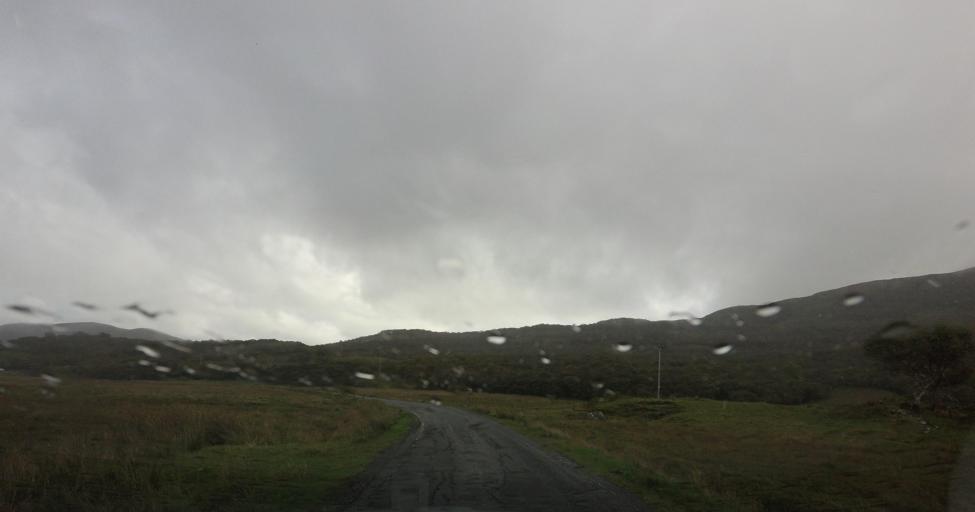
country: GB
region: Scotland
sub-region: Highland
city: Portree
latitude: 57.2082
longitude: -5.9706
